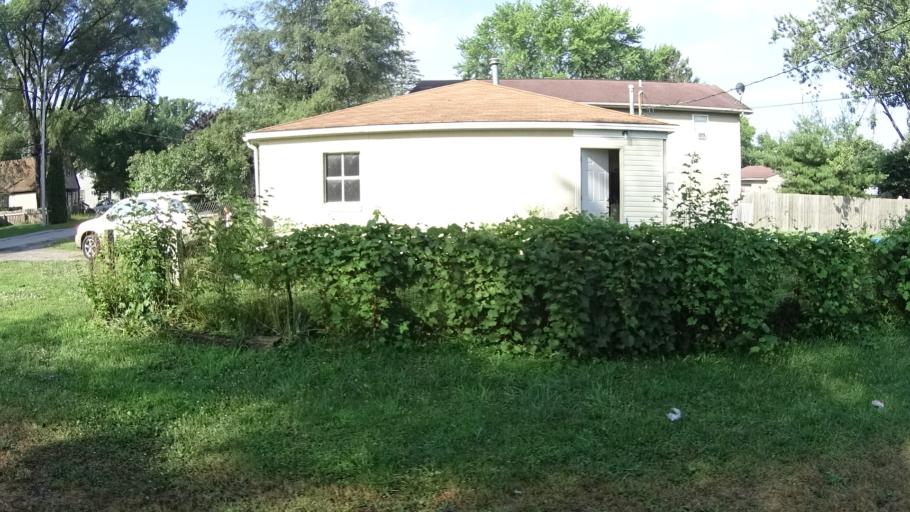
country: US
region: Ohio
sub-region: Erie County
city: Sandusky
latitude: 41.4367
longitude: -82.6838
